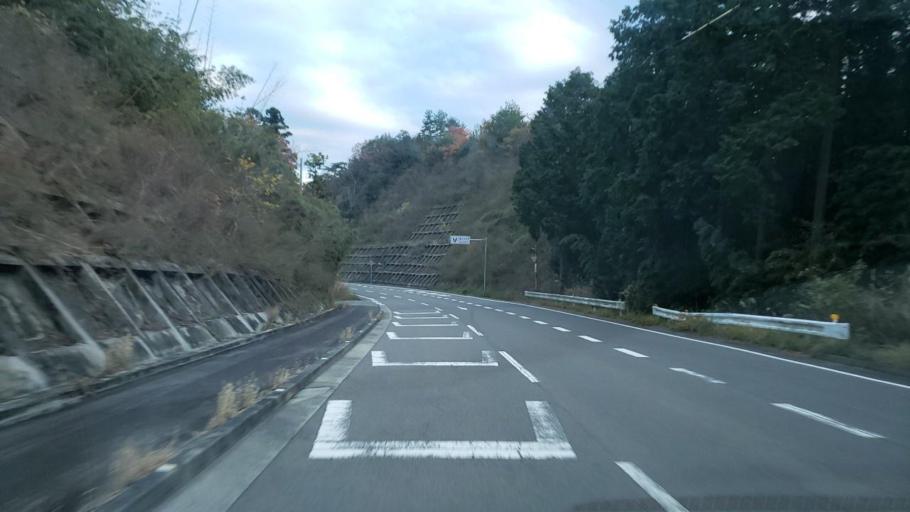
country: JP
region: Kagawa
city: Shido
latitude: 34.1905
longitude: 134.2132
